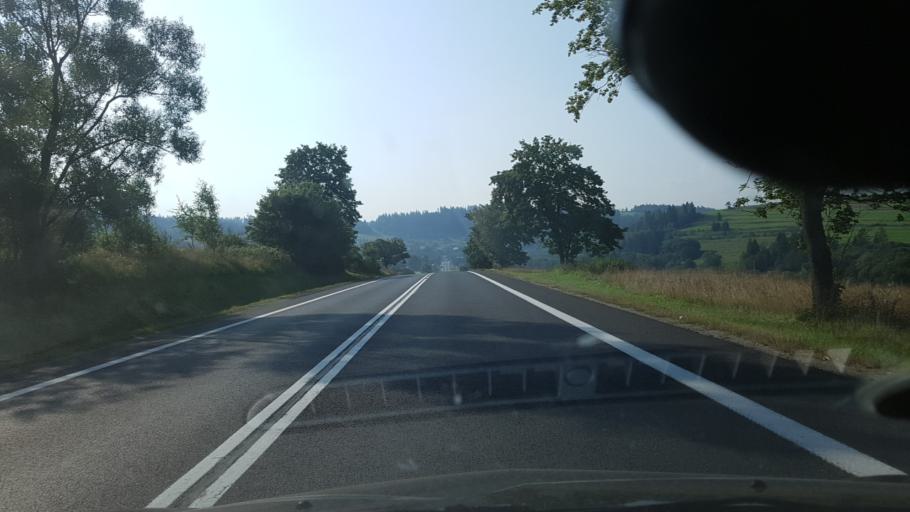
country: PL
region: Lesser Poland Voivodeship
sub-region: Powiat nowotarski
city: Podwilk
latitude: 49.5249
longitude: 19.7144
